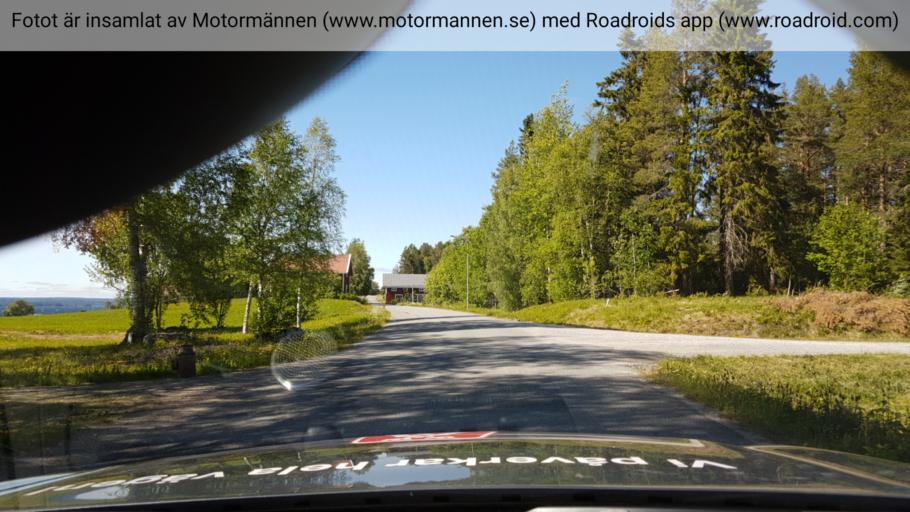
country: SE
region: Jaemtland
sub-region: OEstersunds Kommun
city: Brunflo
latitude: 62.9858
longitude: 14.8886
